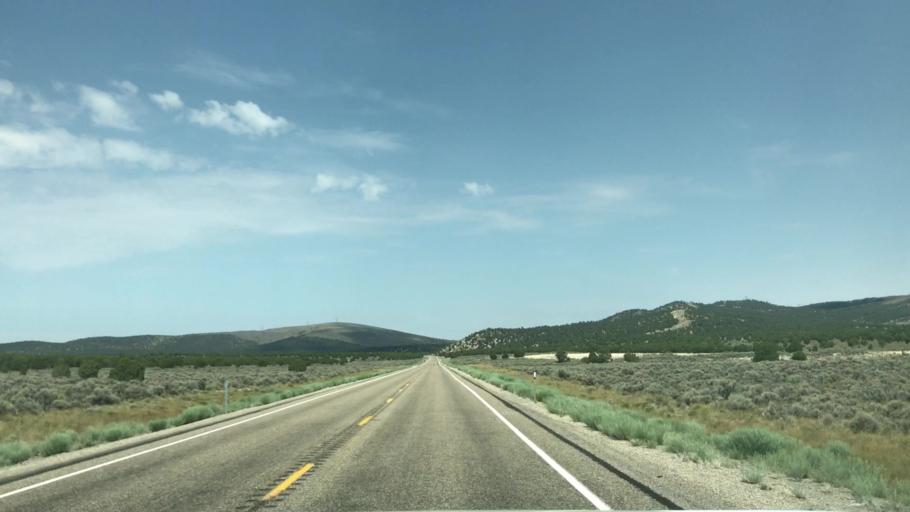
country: US
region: Nevada
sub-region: White Pine County
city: Ely
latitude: 39.3720
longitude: -115.0583
